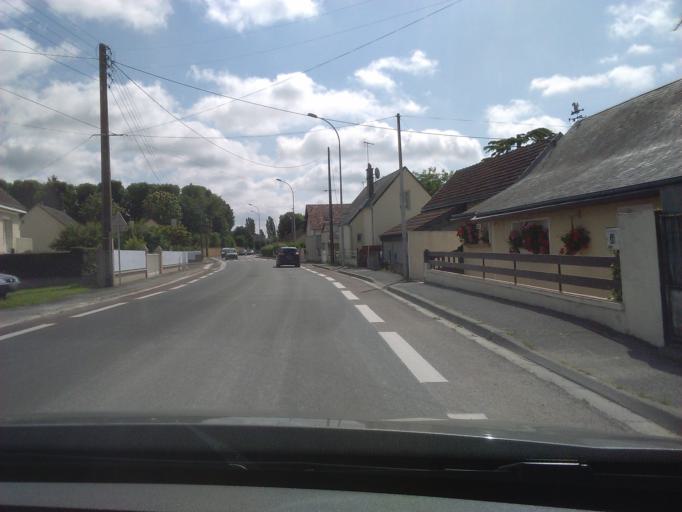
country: FR
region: Centre
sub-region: Departement du Loir-et-Cher
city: Naveil
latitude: 47.8023
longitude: 1.0482
